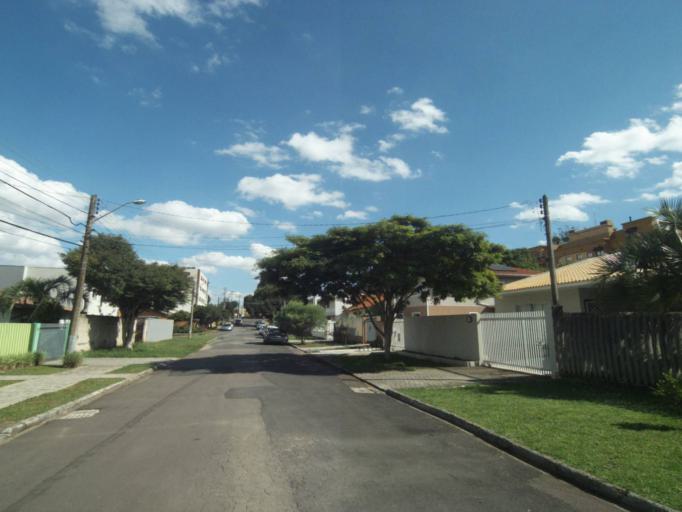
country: BR
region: Parana
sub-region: Curitiba
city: Curitiba
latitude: -25.4445
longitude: -49.3473
